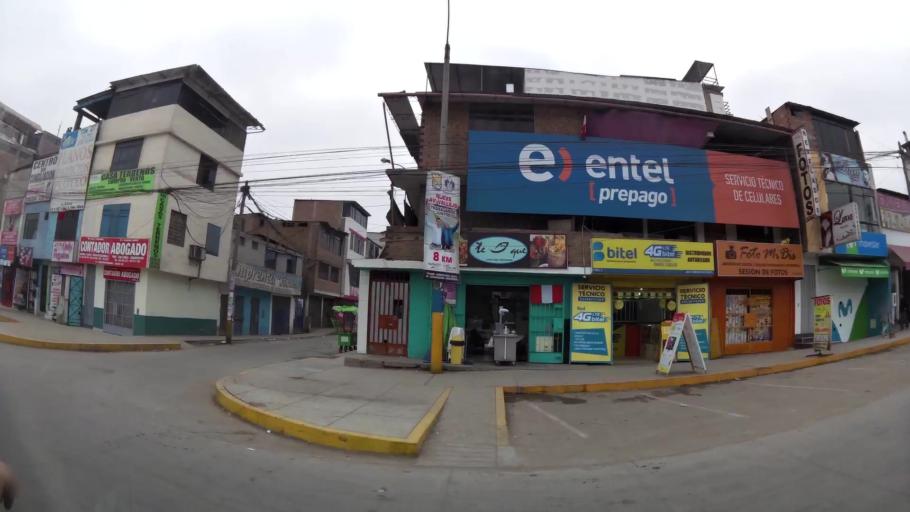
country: PE
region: Lima
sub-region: Lima
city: Surco
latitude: -12.2130
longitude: -76.9362
